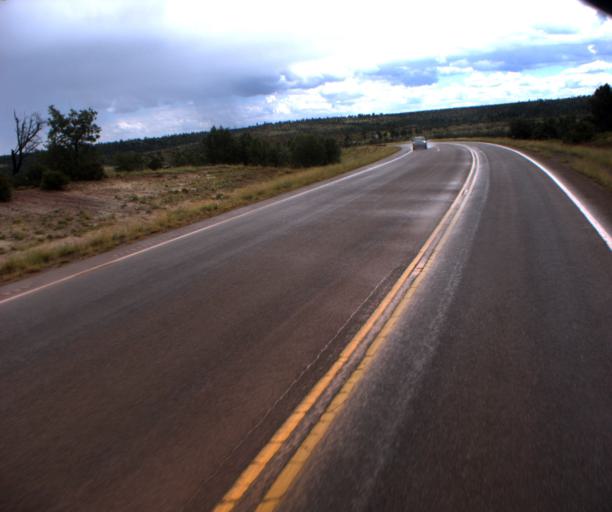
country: US
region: Arizona
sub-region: Navajo County
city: Heber-Overgaard
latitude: 34.3657
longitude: -110.4205
